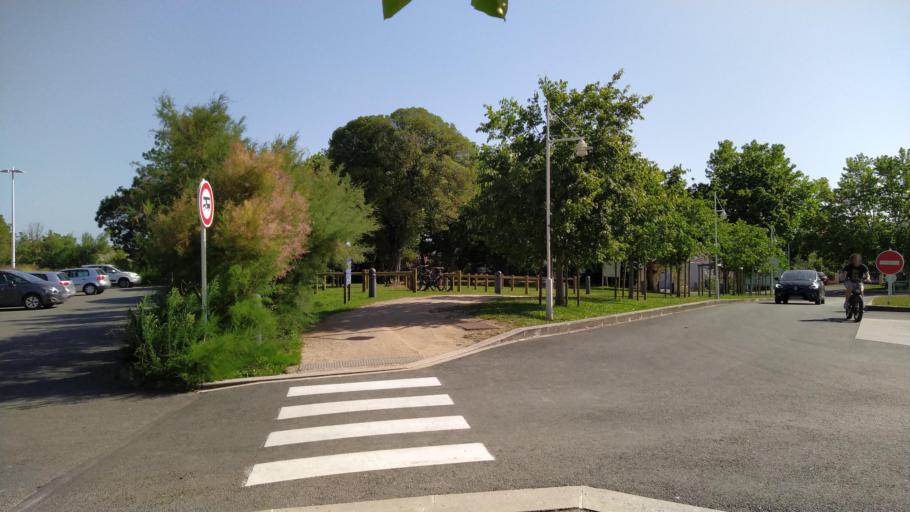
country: FR
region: Poitou-Charentes
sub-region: Departement de la Charente-Maritime
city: Saint-Trojan-les-Bains
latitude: 45.8852
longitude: -1.1948
